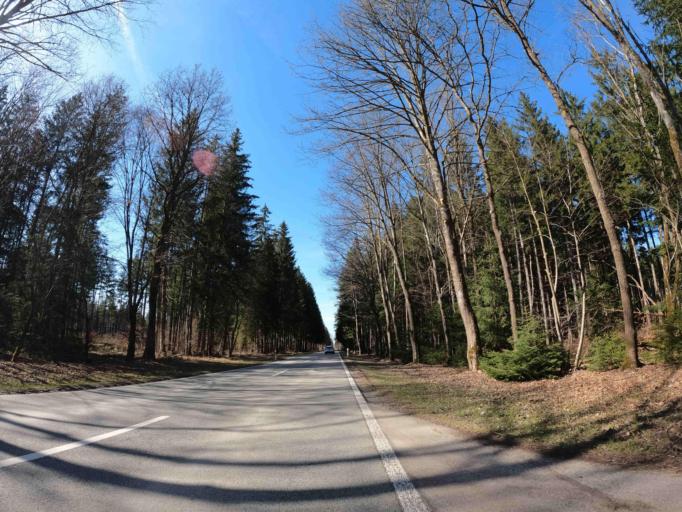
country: DE
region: Bavaria
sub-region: Upper Bavaria
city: Oberhaching
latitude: 48.0069
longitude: 11.6228
